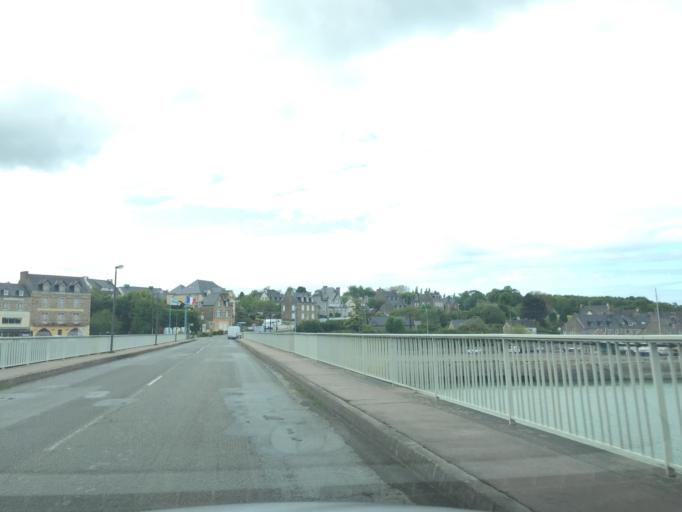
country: FR
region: Brittany
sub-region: Departement des Cotes-d'Armor
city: Crehen
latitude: 48.5734
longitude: -2.2136
